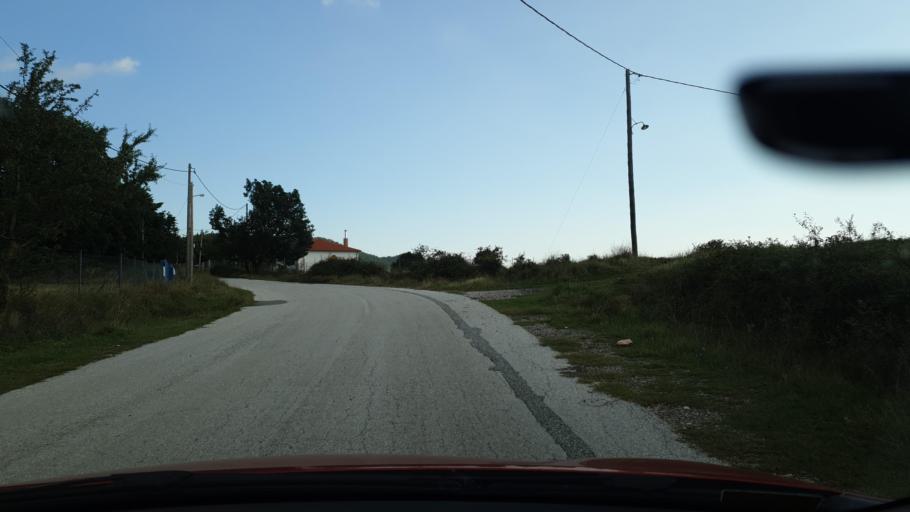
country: GR
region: Central Macedonia
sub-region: Nomos Thessalonikis
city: Peristera
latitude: 40.5198
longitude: 23.2091
